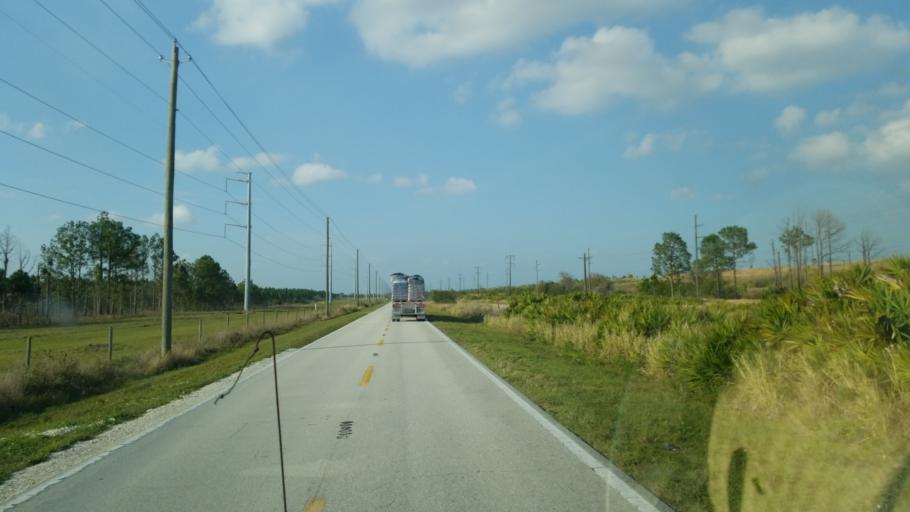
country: US
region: Florida
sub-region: Hardee County
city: Bowling Green
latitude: 27.7032
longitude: -81.9590
